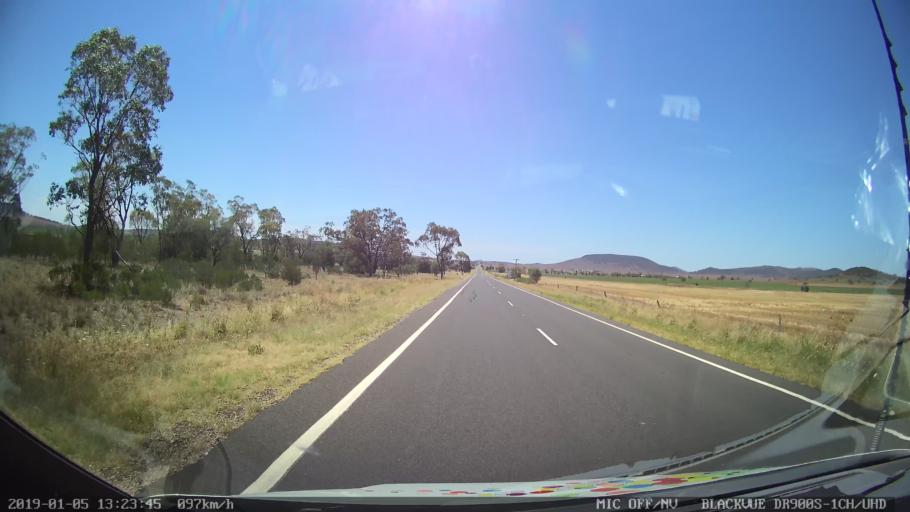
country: AU
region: New South Wales
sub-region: Gunnedah
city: Gunnedah
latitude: -31.0754
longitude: 149.9793
